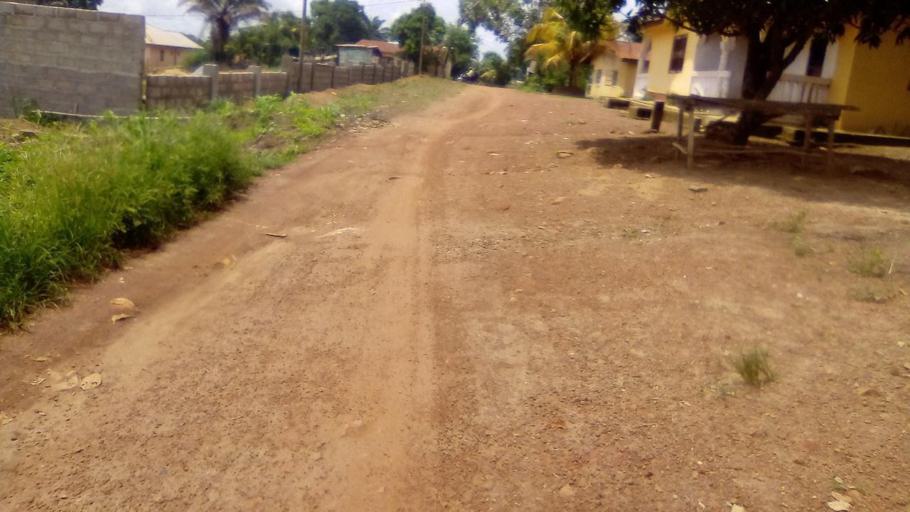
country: SL
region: Southern Province
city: Bo
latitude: 7.9392
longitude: -11.7439
